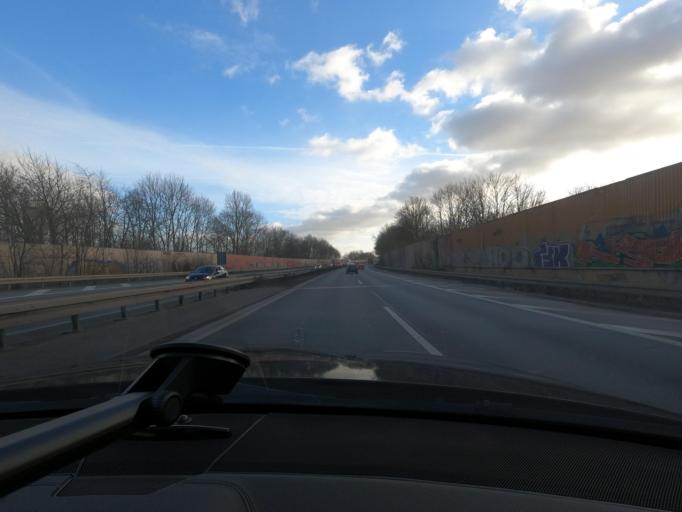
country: DE
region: North Rhine-Westphalia
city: Lanstrop
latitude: 51.5580
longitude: 7.5127
